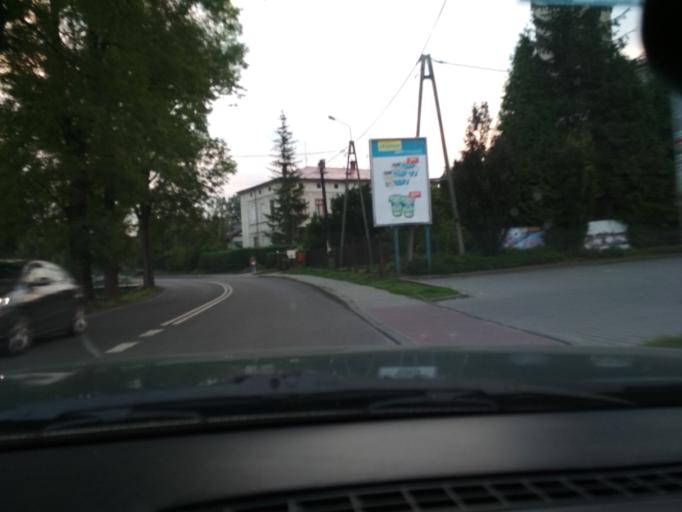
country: PL
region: Silesian Voivodeship
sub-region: Powiat bielski
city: Mazancowice
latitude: 49.8476
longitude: 18.9420
